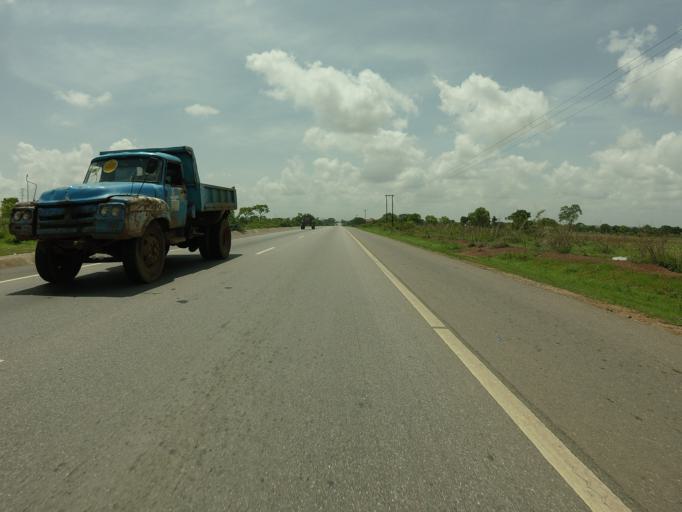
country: GH
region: Northern
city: Tamale
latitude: 9.2960
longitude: -0.9686
